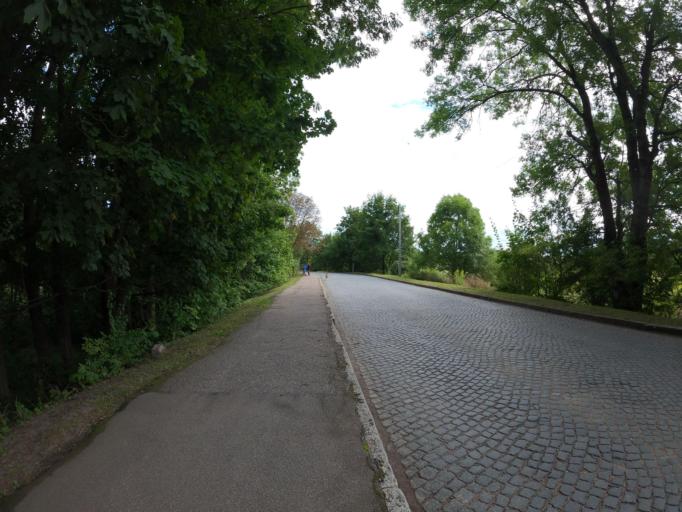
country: RU
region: Kaliningrad
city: Zheleznodorozhnyy
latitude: 54.3538
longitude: 21.3136
